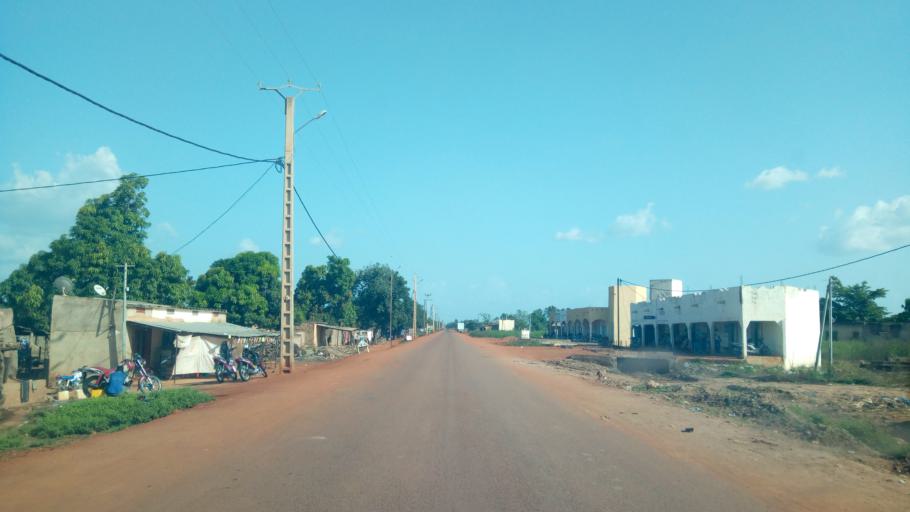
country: ML
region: Sikasso
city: Yorosso
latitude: 12.1810
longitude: -4.8008
